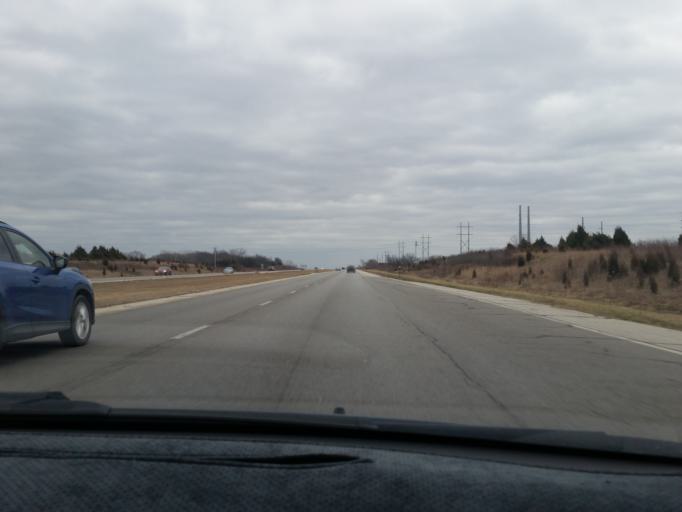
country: US
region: Kansas
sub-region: Johnson County
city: De Soto
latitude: 38.9600
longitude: -94.9507
